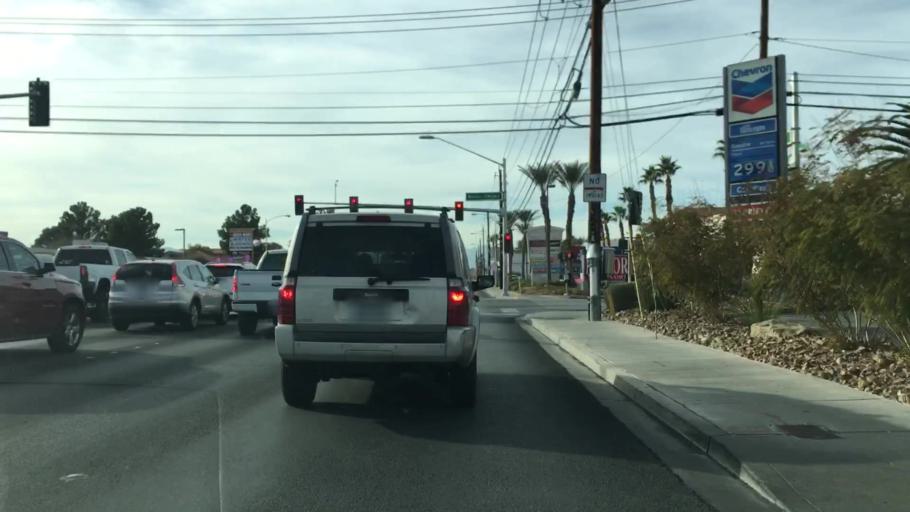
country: US
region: Nevada
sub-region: Clark County
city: Whitney
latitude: 36.0711
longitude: -115.0867
